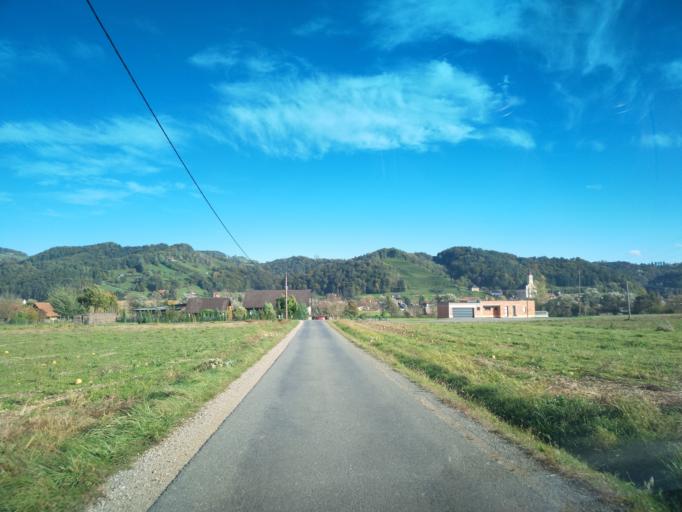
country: AT
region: Styria
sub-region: Politischer Bezirk Leibnitz
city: Sankt Johann im Saggautal
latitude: 46.7079
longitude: 15.3911
